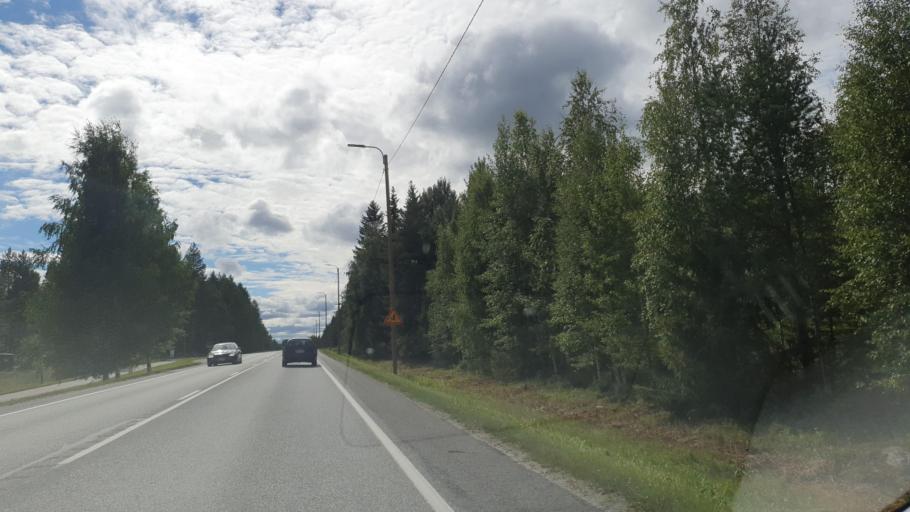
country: FI
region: Kainuu
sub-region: Kajaani
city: Kajaani
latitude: 64.2013
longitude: 27.6384
